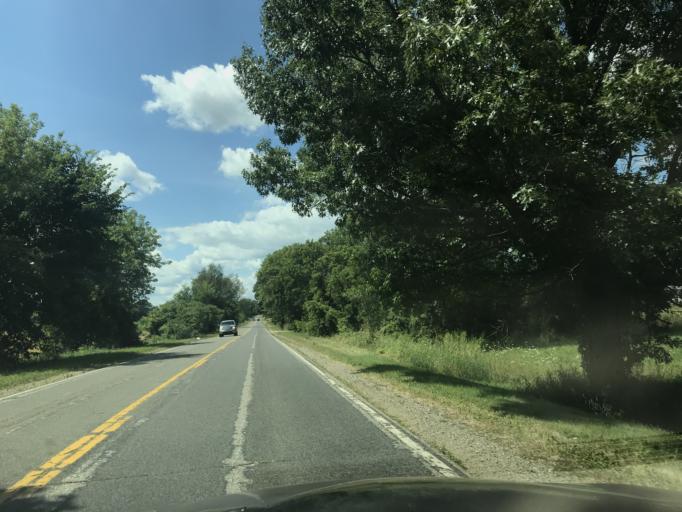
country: US
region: Michigan
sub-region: Ingham County
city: Leslie
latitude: 42.4512
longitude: -84.4550
